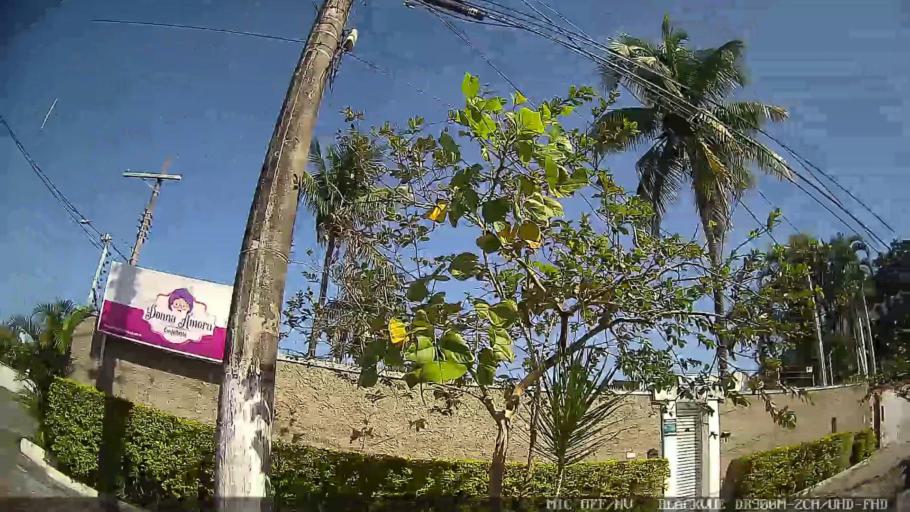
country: BR
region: Sao Paulo
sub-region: Guaruja
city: Guaruja
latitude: -23.9897
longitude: -46.2449
